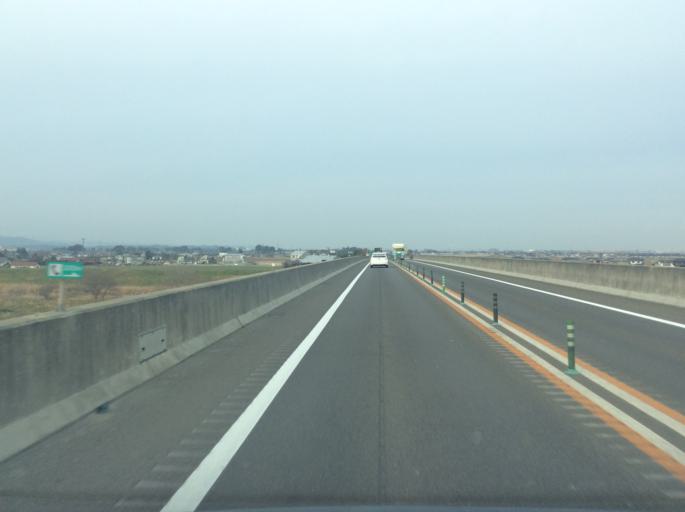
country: JP
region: Miyagi
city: Iwanuma
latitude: 38.0954
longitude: 140.8880
